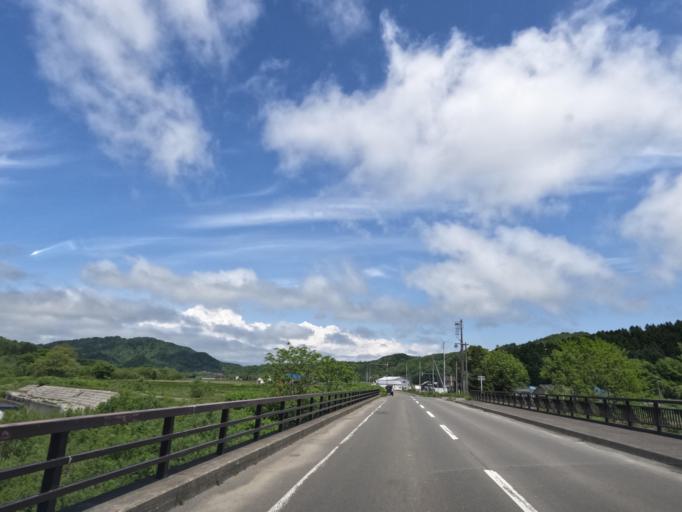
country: JP
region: Hokkaido
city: Tobetsu
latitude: 43.2980
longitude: 141.5452
